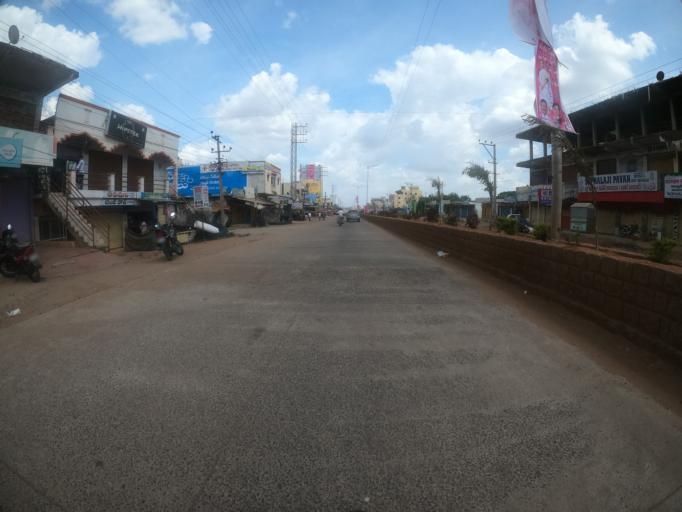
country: IN
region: Telangana
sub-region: Rangareddi
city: Sriramnagar
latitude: 17.3121
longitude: 78.1403
